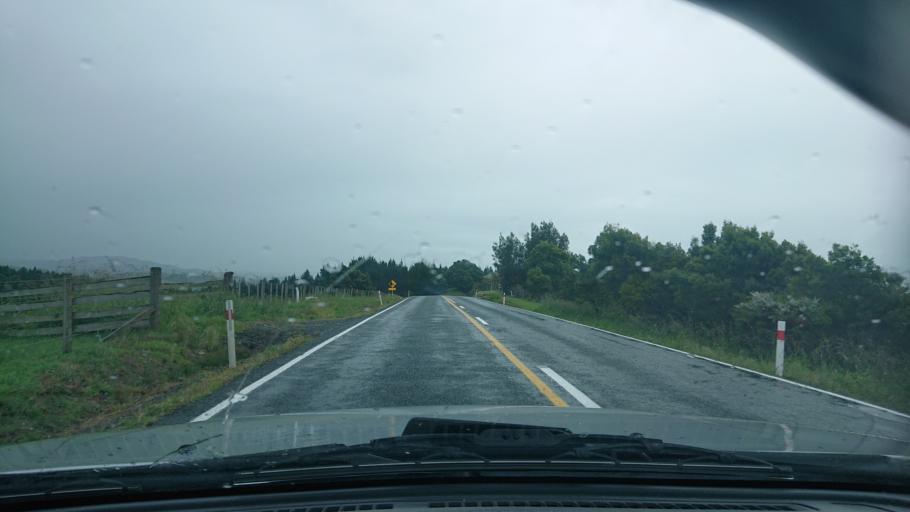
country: NZ
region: Auckland
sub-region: Auckland
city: Wellsford
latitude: -36.3576
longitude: 174.4689
